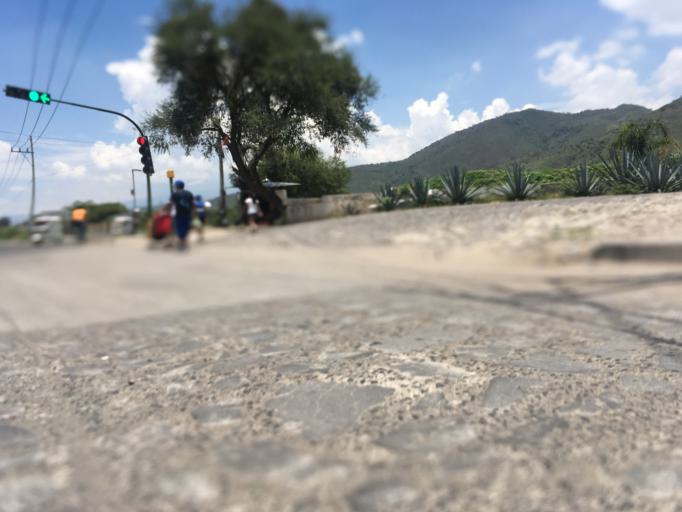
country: MX
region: Jalisco
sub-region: Tlajomulco de Zuniga
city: Jardines de San Sebastian
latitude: 20.5261
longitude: -103.4247
